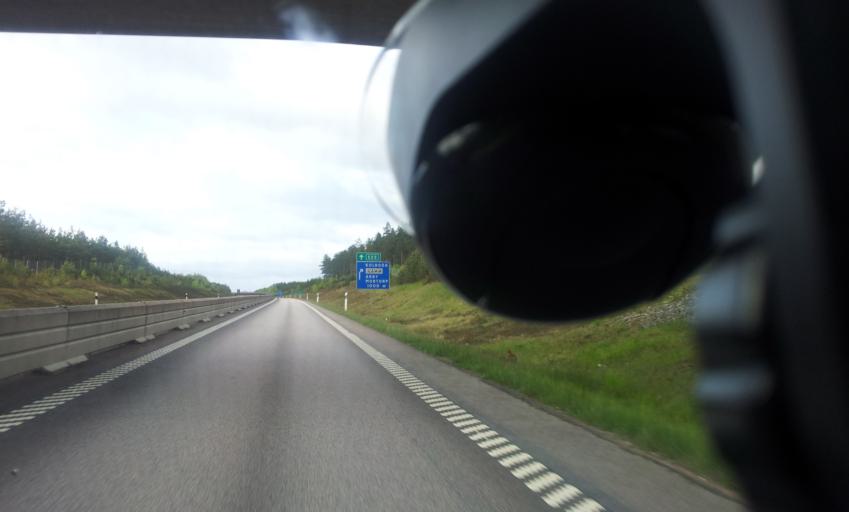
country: SE
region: Kalmar
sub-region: Kalmar Kommun
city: Ljungbyholm
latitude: 56.6009
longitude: 16.1303
